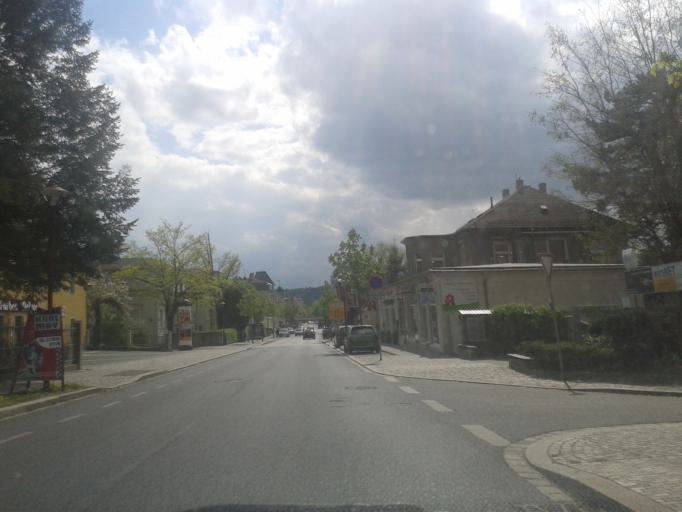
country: DE
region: Saxony
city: Radebeul
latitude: 51.1101
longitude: 13.6317
